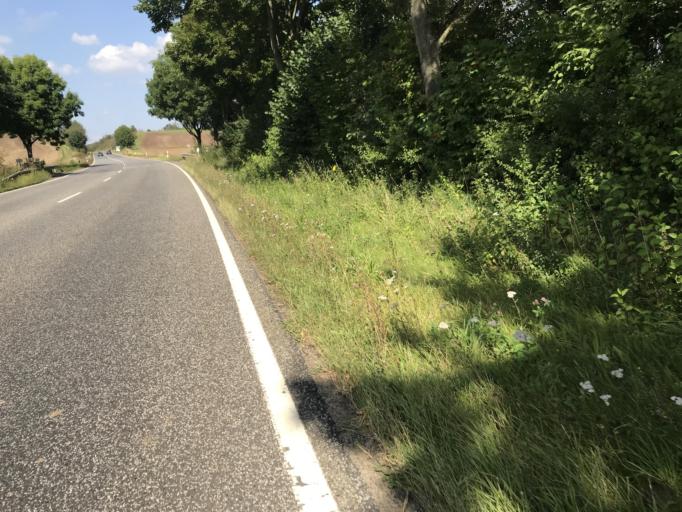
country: DE
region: Hesse
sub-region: Regierungsbezirk Giessen
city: Hungen
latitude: 50.4526
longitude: 8.9406
